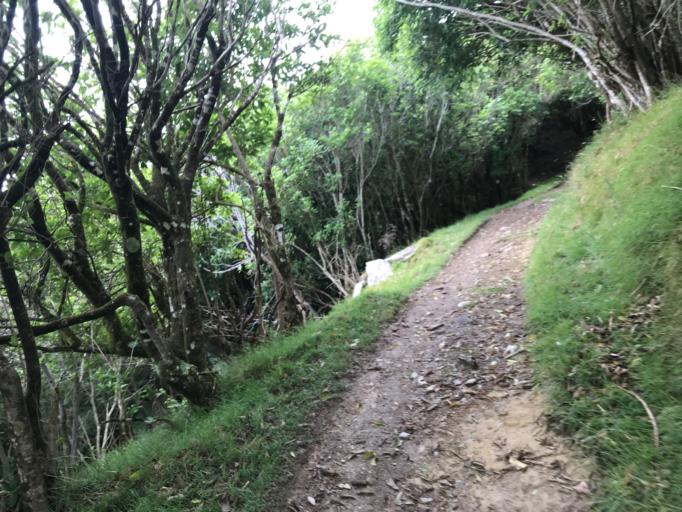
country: NZ
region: Marlborough
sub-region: Marlborough District
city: Picton
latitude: -41.2319
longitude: 173.9579
